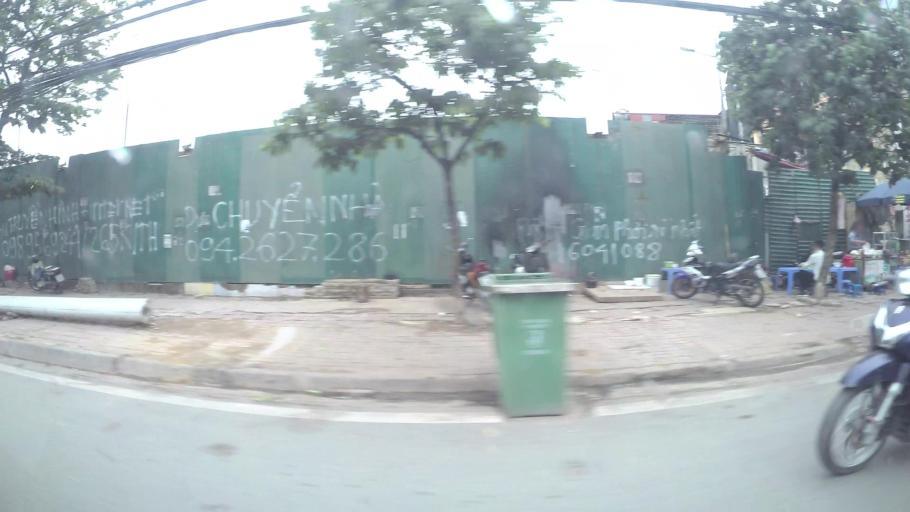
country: VN
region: Ha Noi
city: Hai BaTrung
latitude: 21.0059
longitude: 105.8609
